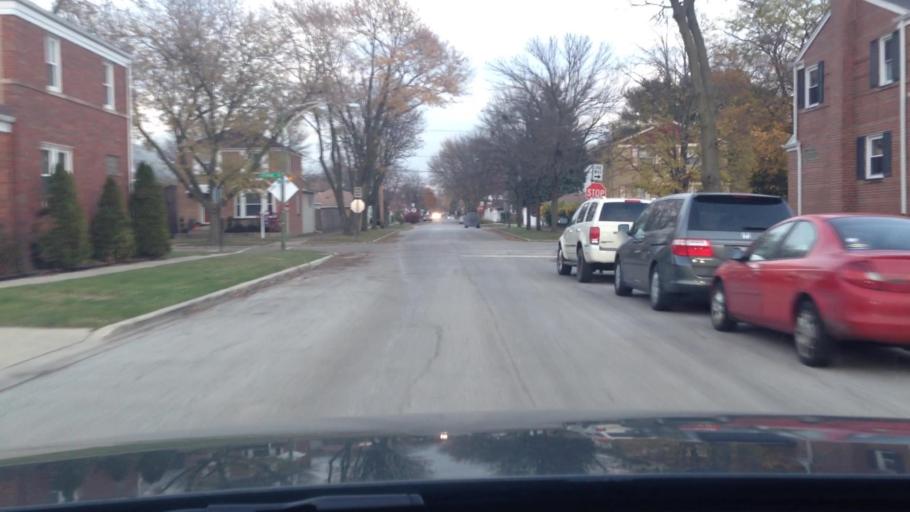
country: US
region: Illinois
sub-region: Cook County
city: Norridge
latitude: 41.9466
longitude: -87.8358
